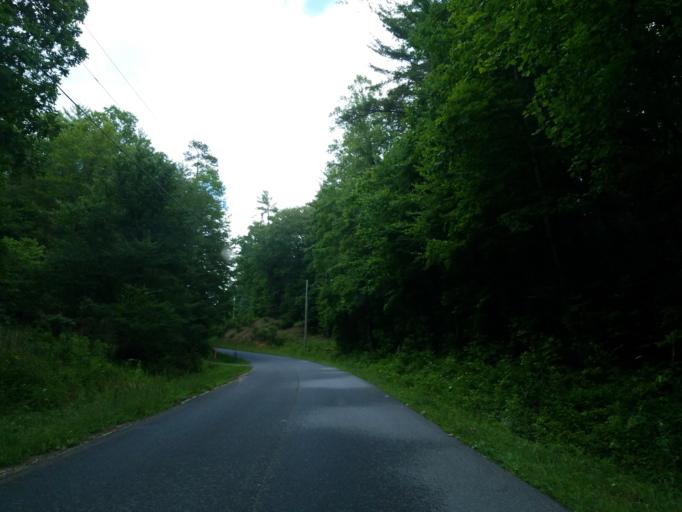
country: US
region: Georgia
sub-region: Fannin County
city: Blue Ridge
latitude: 34.7767
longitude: -84.3760
